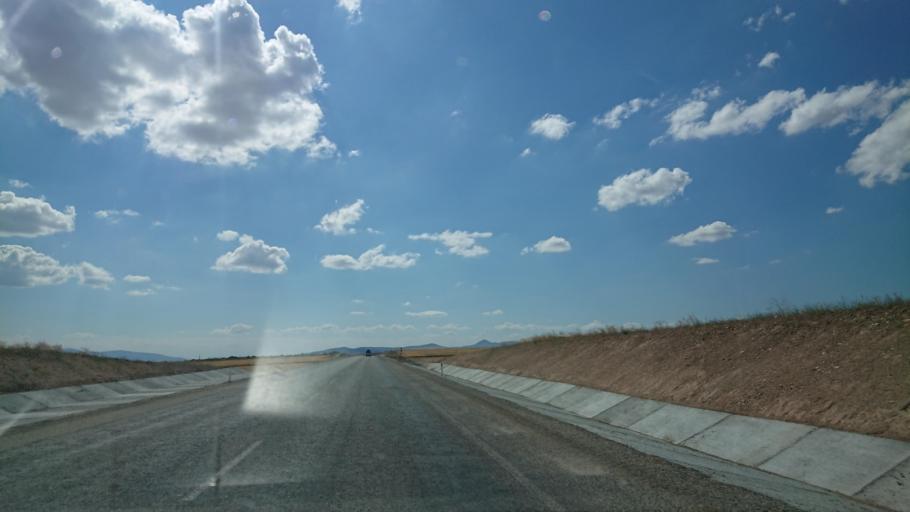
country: TR
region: Kirsehir
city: Kirsehir
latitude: 39.1227
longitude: 34.0025
